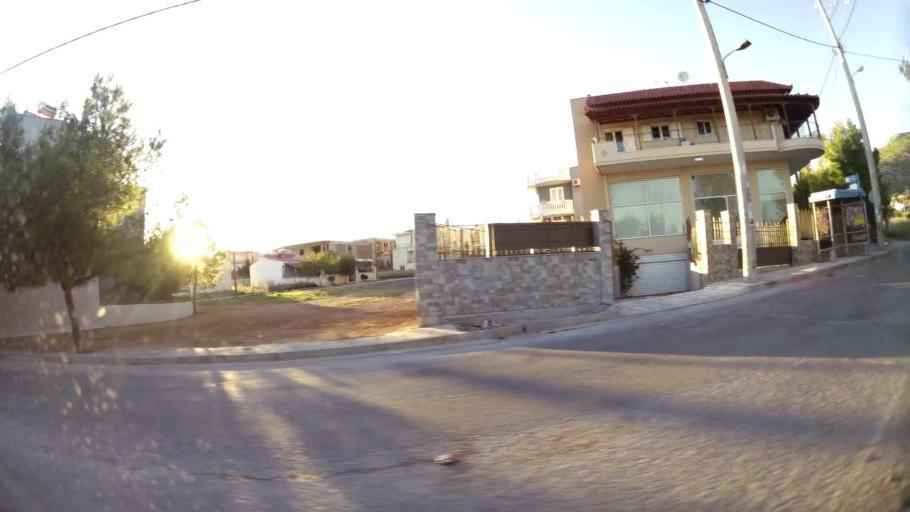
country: GR
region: Attica
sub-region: Nomarchia Dytikis Attikis
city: Ano Liosia
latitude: 38.0938
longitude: 23.7003
